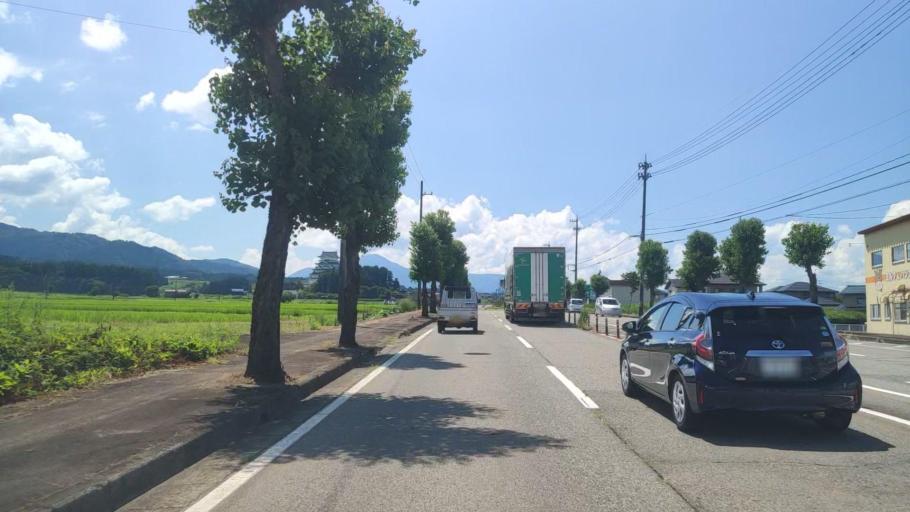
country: JP
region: Fukui
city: Katsuyama
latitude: 36.0490
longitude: 136.5151
